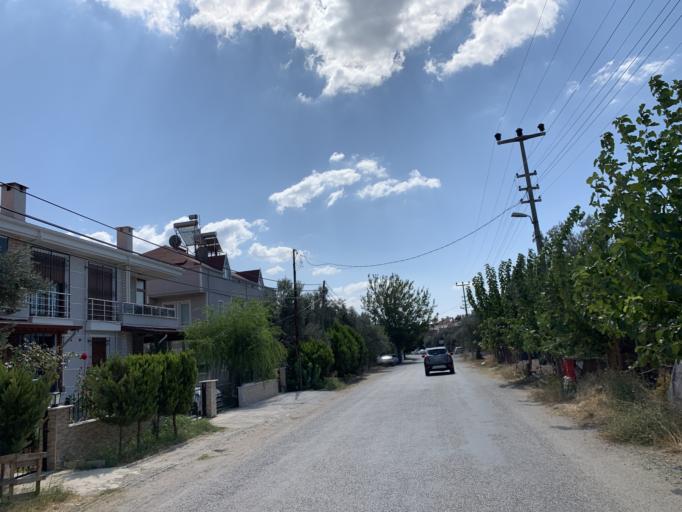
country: TR
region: Balikesir
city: Altinoluk
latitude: 39.5691
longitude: 26.8355
